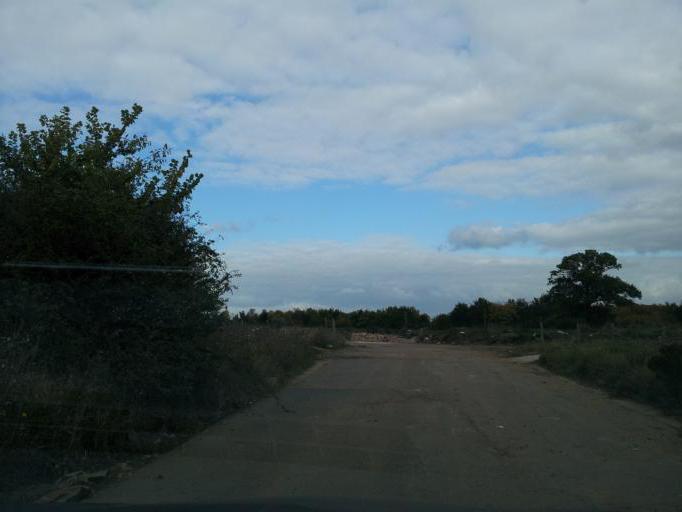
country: GB
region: England
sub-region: Milton Keynes
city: Shenley Church End
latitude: 51.9949
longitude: -0.7983
